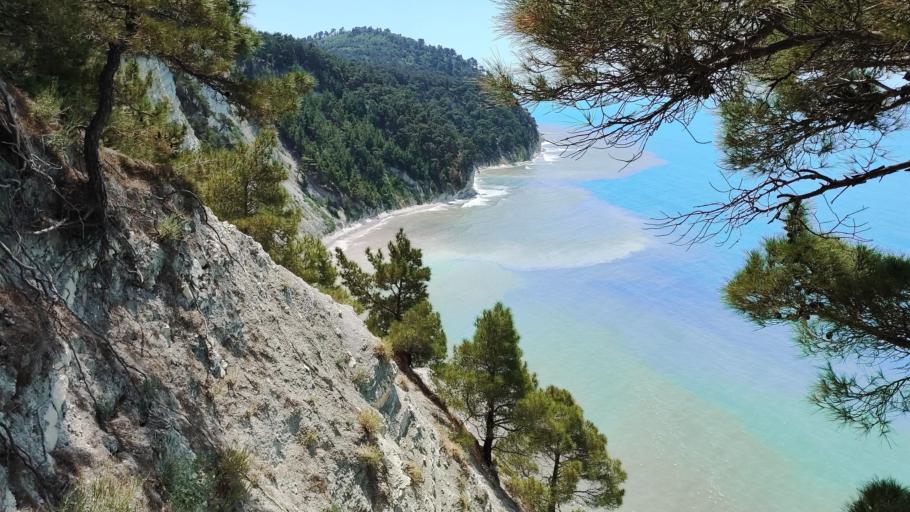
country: RU
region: Krasnodarskiy
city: Divnomorskoye
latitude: 44.4788
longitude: 38.1408
